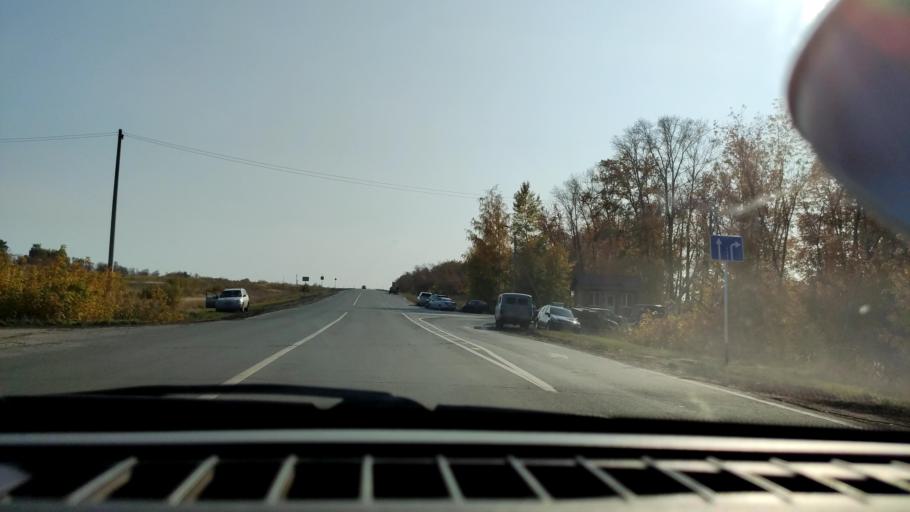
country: RU
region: Samara
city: Dubovyy Umet
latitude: 53.0946
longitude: 50.3496
